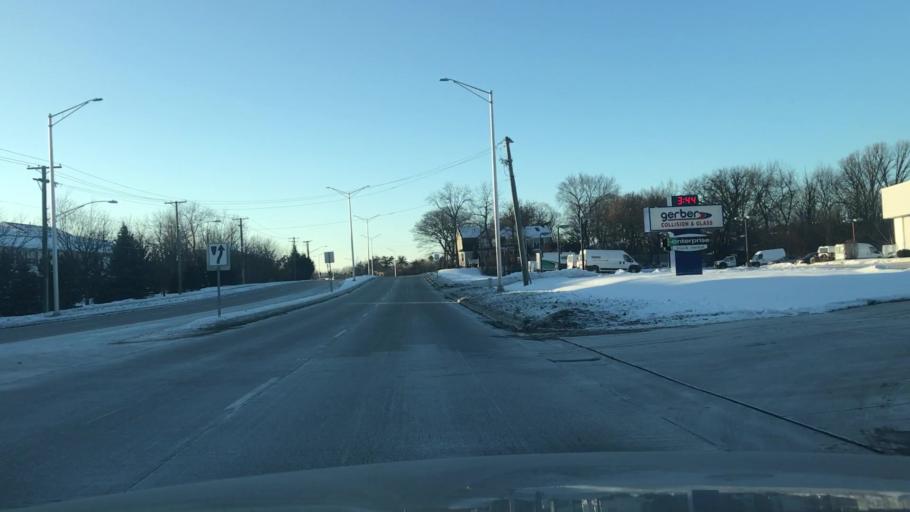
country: US
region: Illinois
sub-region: Kane County
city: Aurora
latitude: 41.7597
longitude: -88.2558
